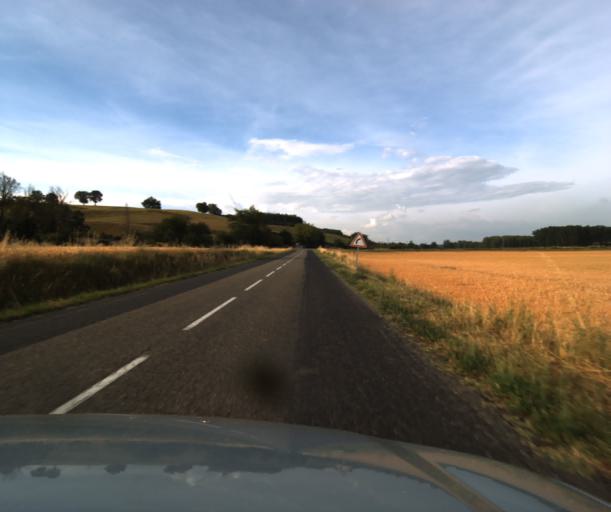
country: FR
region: Midi-Pyrenees
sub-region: Departement du Tarn-et-Garonne
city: Castelsarrasin
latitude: 43.9621
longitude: 1.1055
